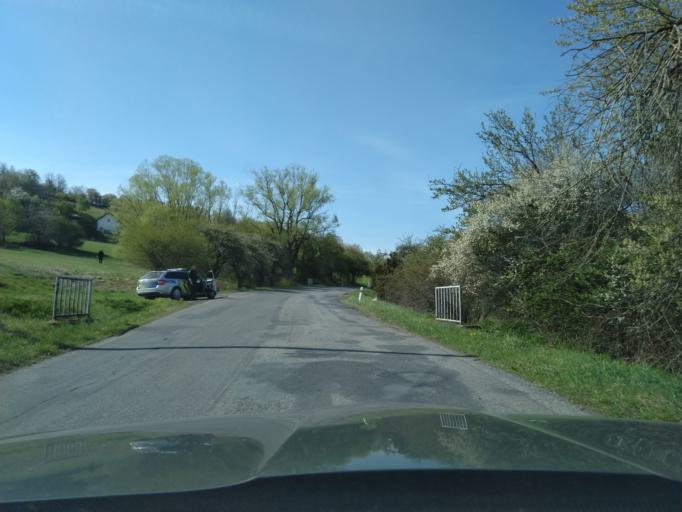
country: CZ
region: Plzensky
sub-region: Okres Klatovy
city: Susice
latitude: 49.2367
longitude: 13.5355
